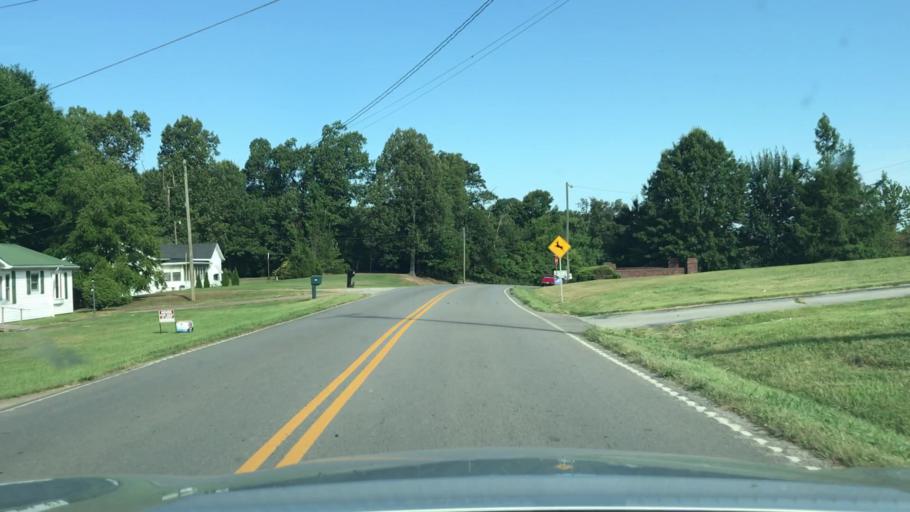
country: US
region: Kentucky
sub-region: Muhlenberg County
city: Greenville
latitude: 37.1892
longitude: -87.1700
